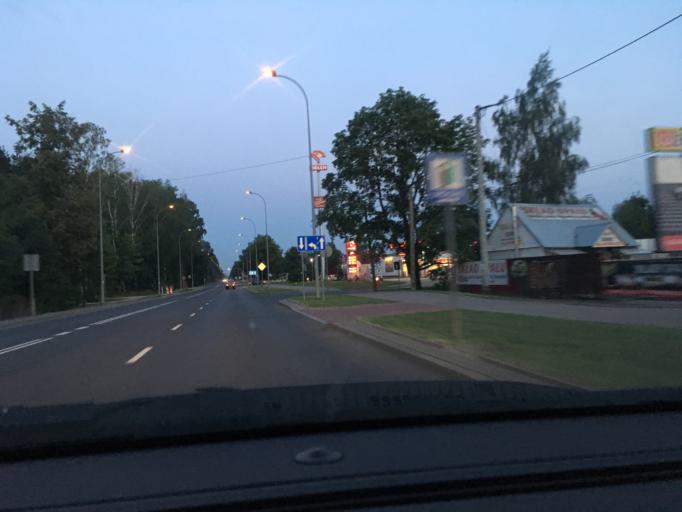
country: PL
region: Podlasie
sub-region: Bialystok
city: Bialystok
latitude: 53.1079
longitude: 23.2124
